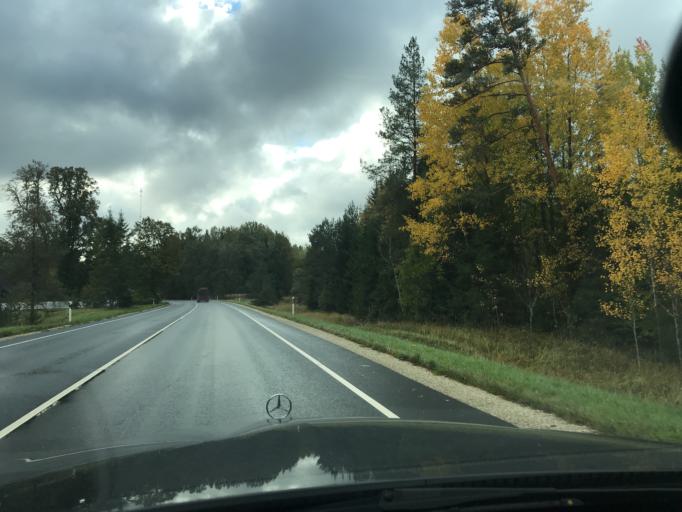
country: EE
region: Viljandimaa
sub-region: Karksi vald
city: Karksi-Nuia
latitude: 58.0276
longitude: 25.6543
